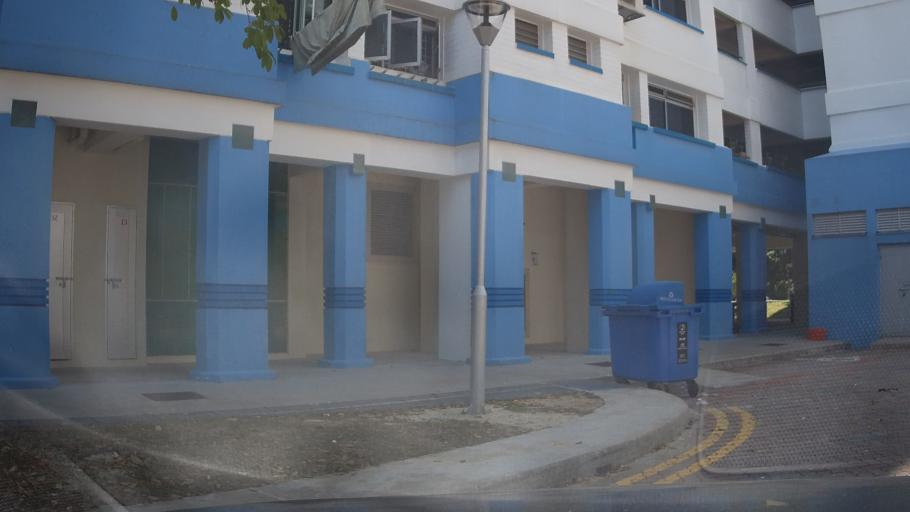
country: MY
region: Johor
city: Kampung Pasir Gudang Baru
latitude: 1.3682
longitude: 103.9629
